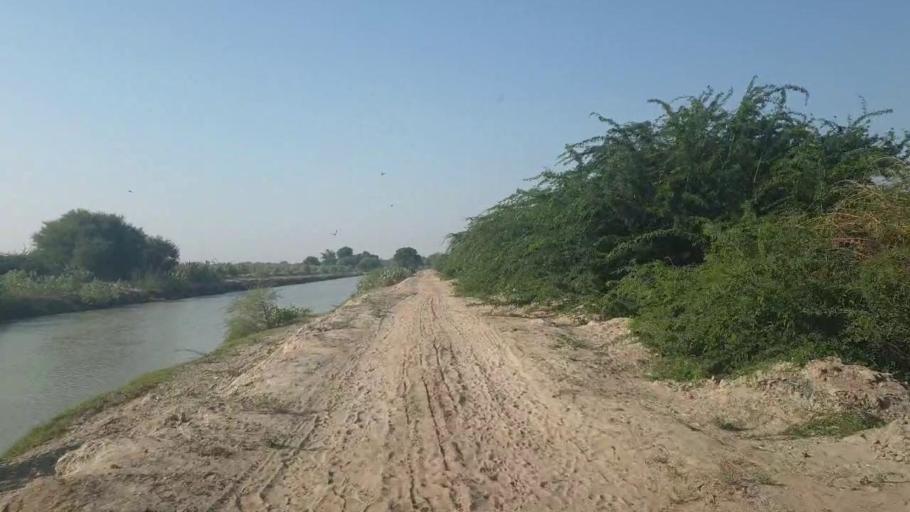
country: PK
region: Sindh
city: Tando Bago
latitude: 24.7212
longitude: 68.9184
